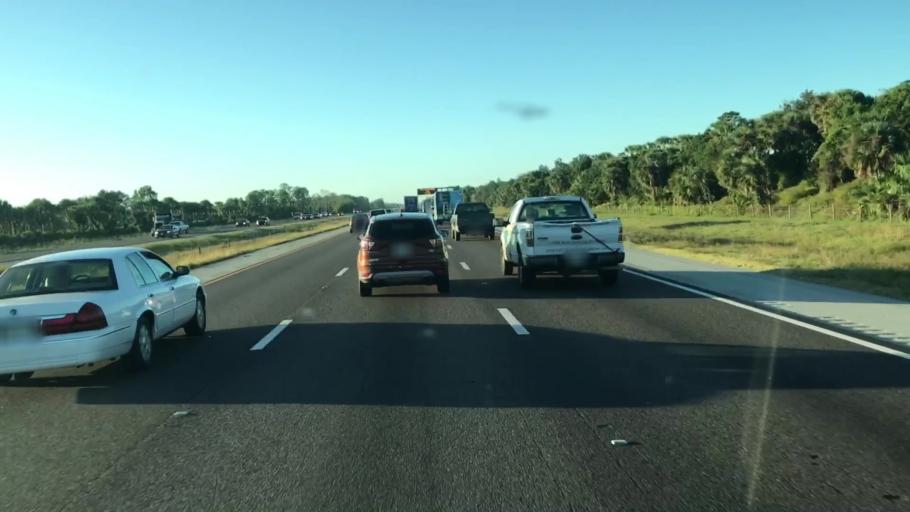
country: US
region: Florida
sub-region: Lee County
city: Bonita Springs
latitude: 26.2989
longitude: -81.7434
